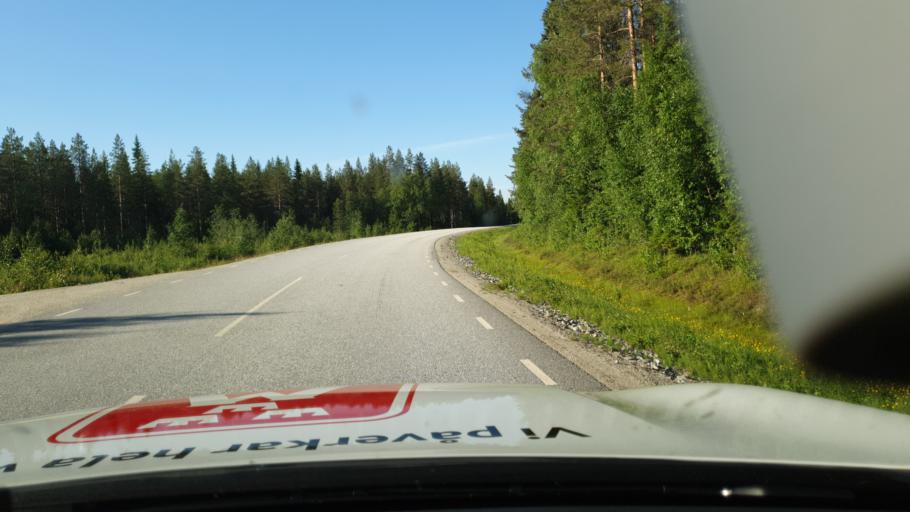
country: SE
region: Vaesterbotten
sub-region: Bjurholms Kommun
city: Bjurholm
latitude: 64.1768
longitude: 19.4012
